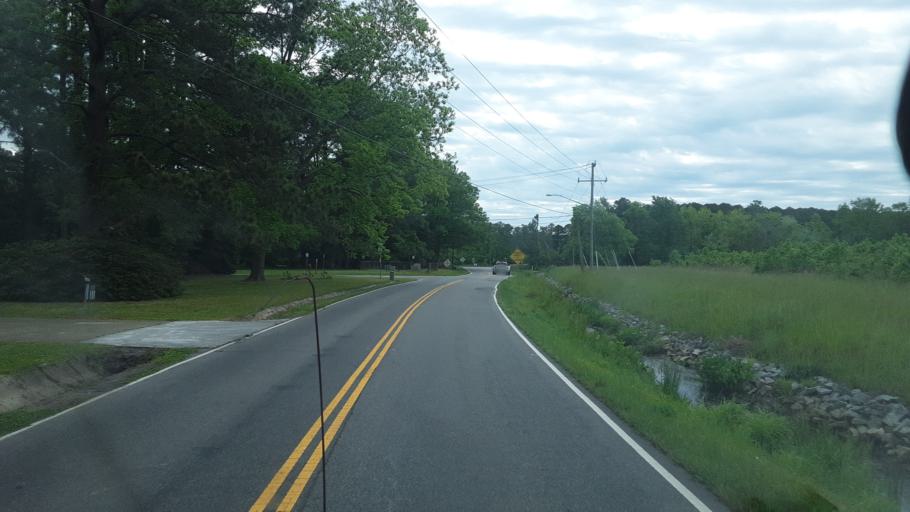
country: US
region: Virginia
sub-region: City of Virginia Beach
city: Virginia Beach
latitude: 36.7331
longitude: -75.9877
